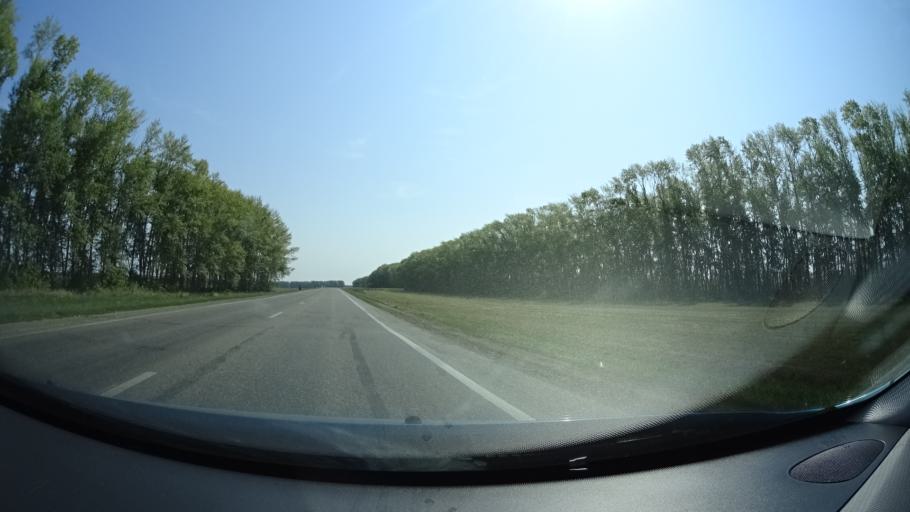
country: RU
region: Bashkortostan
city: Karmaskaly
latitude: 54.3906
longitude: 56.1233
